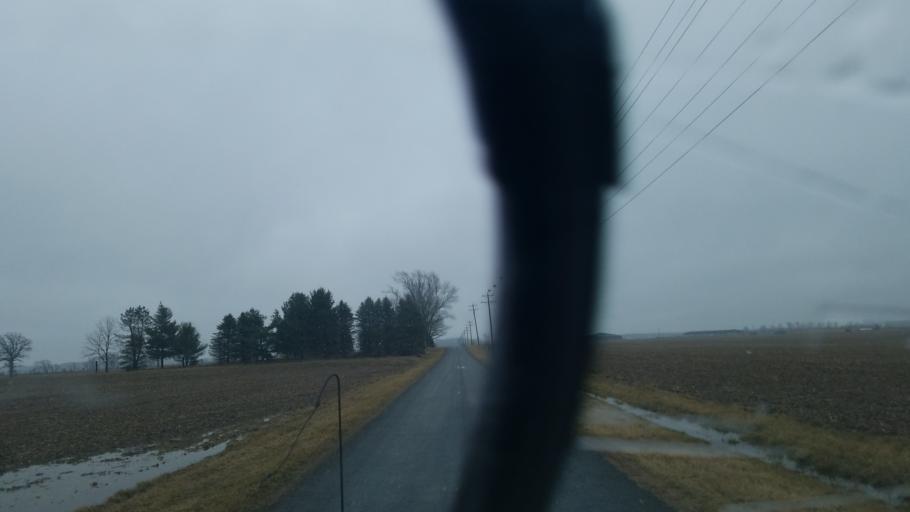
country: US
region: Ohio
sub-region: Union County
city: New California
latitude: 40.2026
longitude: -83.2673
